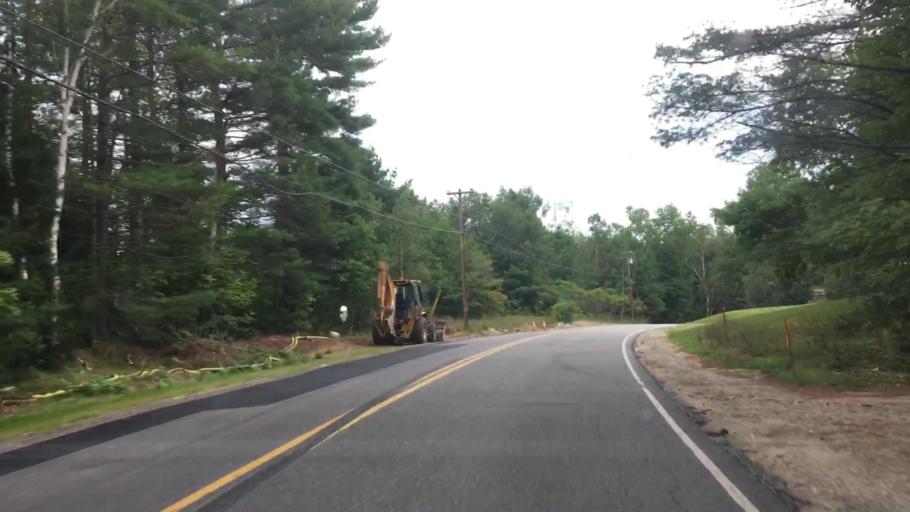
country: US
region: Maine
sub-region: Oxford County
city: Rumford
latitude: 44.5240
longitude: -70.6812
